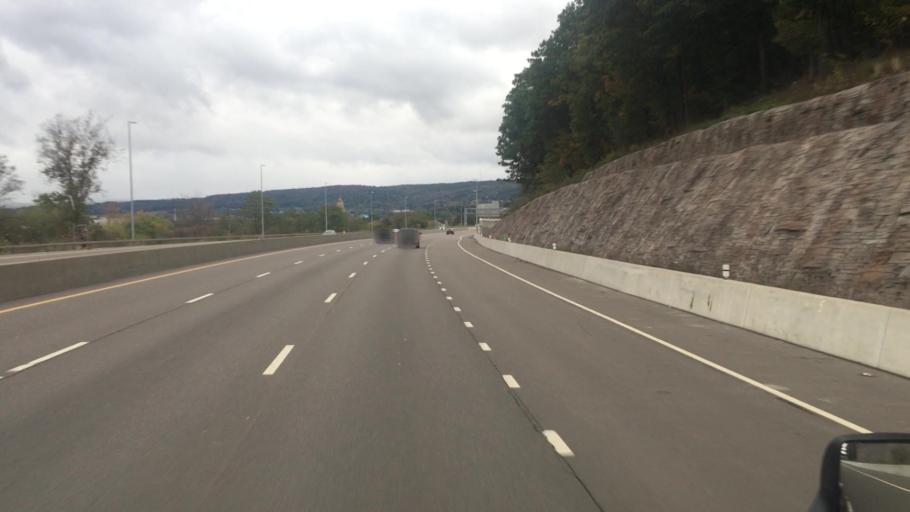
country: US
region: New York
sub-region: Broome County
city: Binghamton
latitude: 42.1155
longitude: -75.9347
